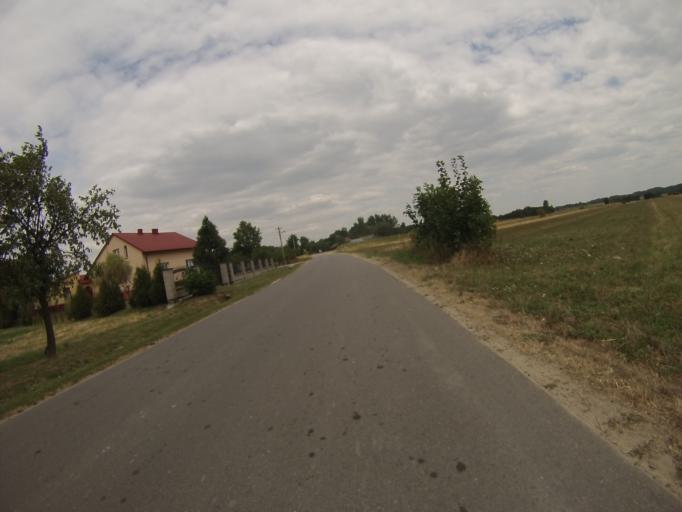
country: PL
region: Swietokrzyskie
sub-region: Powiat staszowski
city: Bogoria
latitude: 50.6841
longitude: 21.1985
